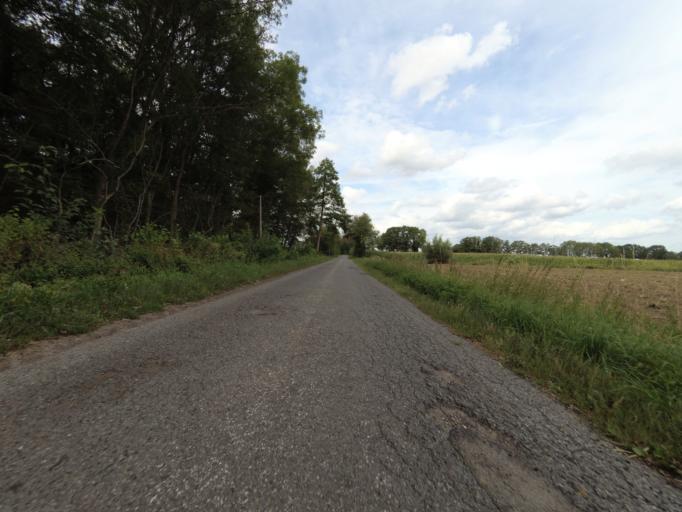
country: DE
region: North Rhine-Westphalia
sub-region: Regierungsbezirk Munster
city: Ahaus
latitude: 52.1360
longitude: 7.0003
